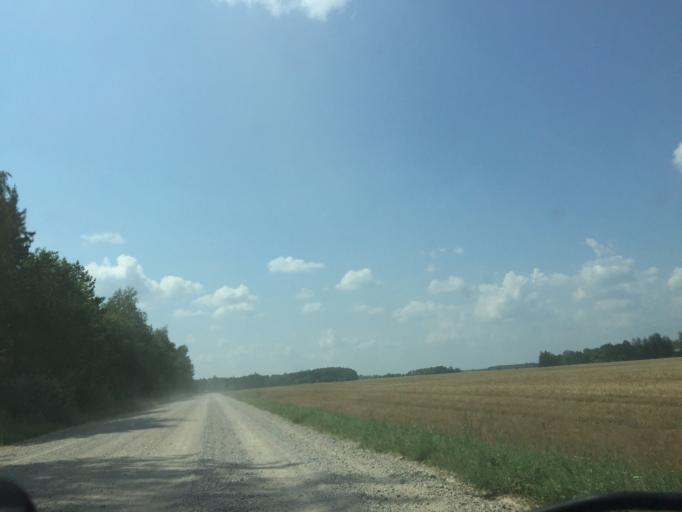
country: LT
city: Zagare
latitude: 56.3788
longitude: 23.2858
